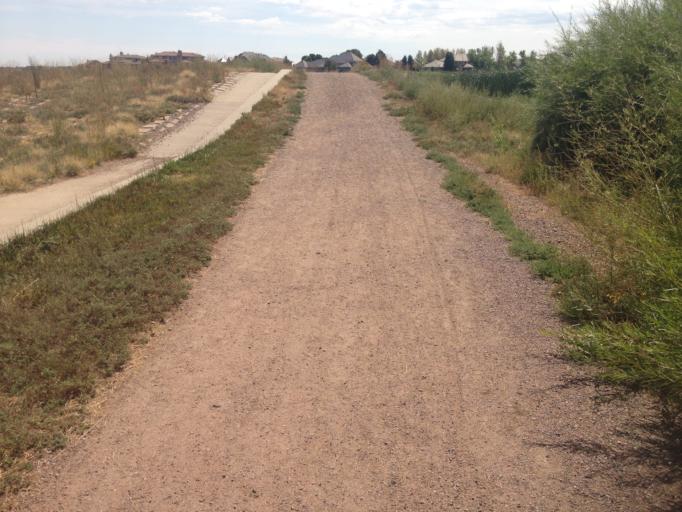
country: US
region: Colorado
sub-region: Adams County
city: Northglenn
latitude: 39.9565
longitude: -105.0088
